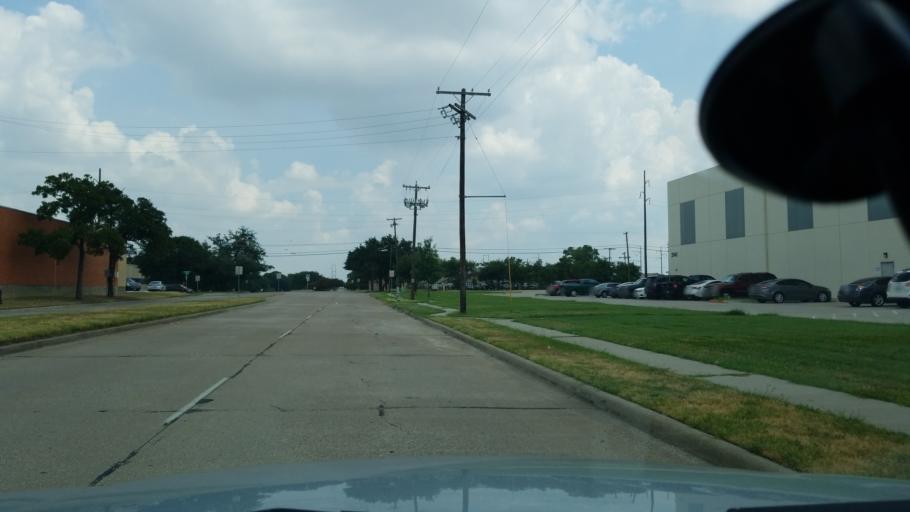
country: US
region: Texas
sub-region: Dallas County
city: Irving
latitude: 32.8357
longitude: -96.8932
